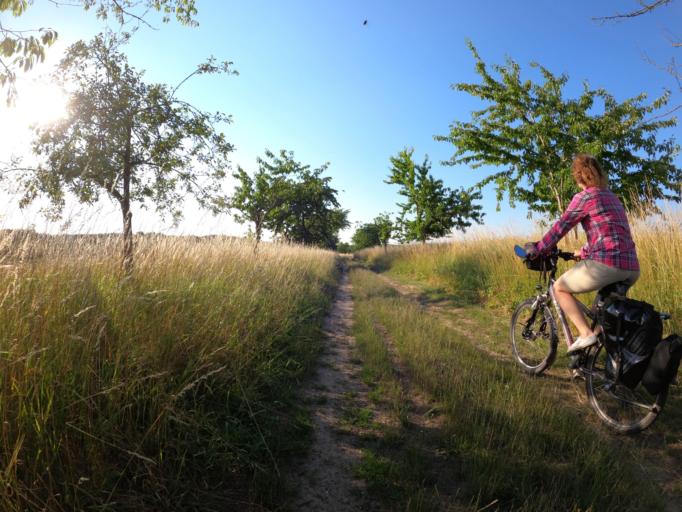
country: DE
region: Brandenburg
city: Tantow
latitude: 53.2439
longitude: 14.3681
